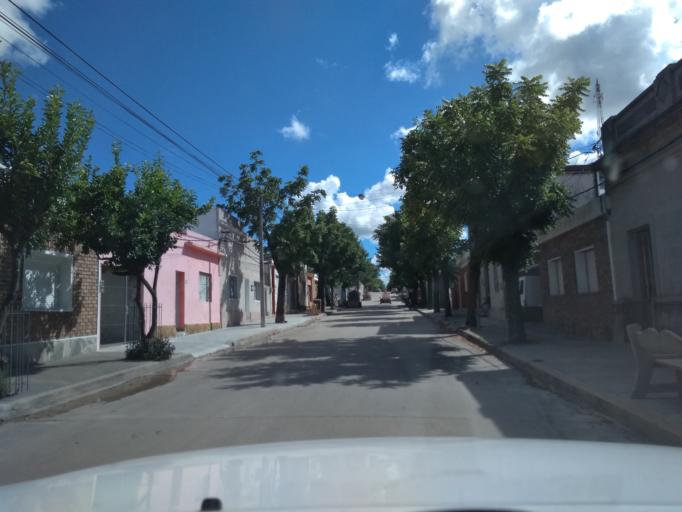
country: UY
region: Florida
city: Florida
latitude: -34.0977
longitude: -56.2104
